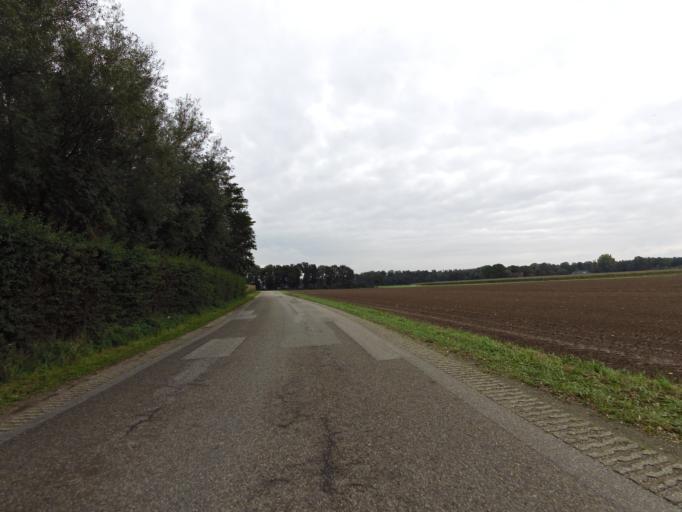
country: NL
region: Gelderland
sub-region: Oude IJsselstreek
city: Gendringen
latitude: 51.8757
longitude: 6.4105
